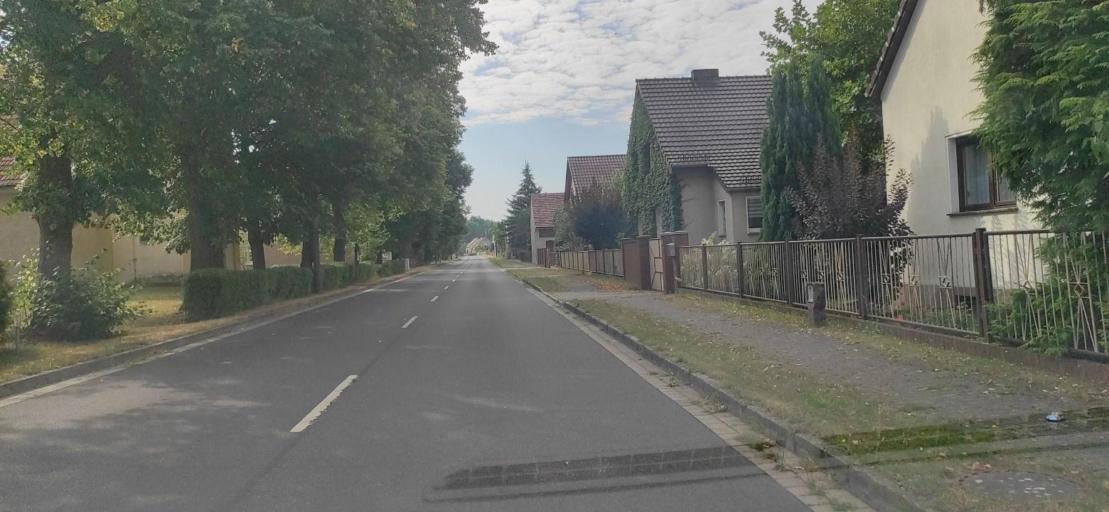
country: DE
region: Brandenburg
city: Forst
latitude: 51.6919
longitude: 14.7160
